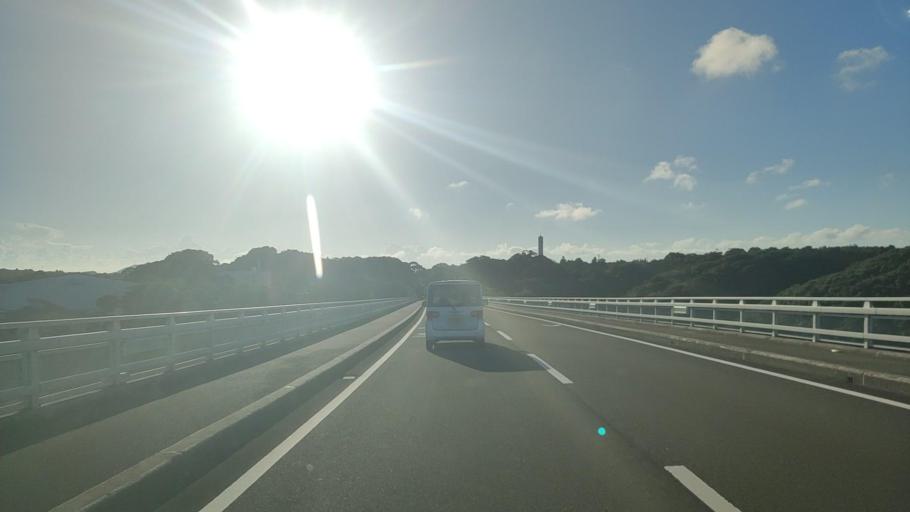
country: JP
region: Mie
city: Toba
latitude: 34.2667
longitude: 136.8123
